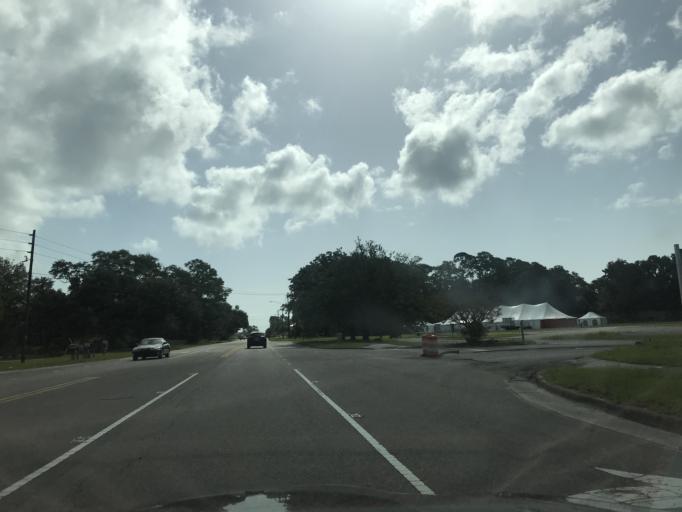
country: US
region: North Carolina
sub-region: New Hanover County
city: Seagate
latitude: 34.2204
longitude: -77.8261
